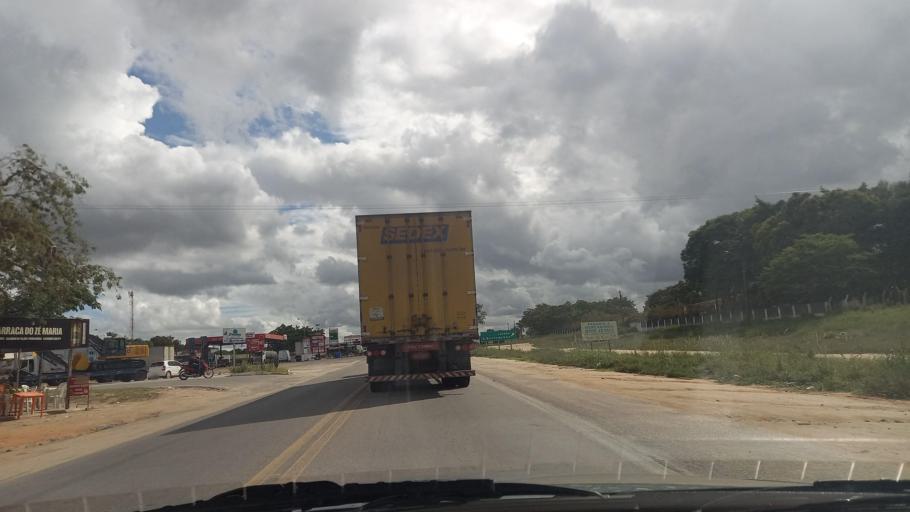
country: BR
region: Pernambuco
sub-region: Lajedo
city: Lajedo
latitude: -8.6580
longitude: -36.3282
